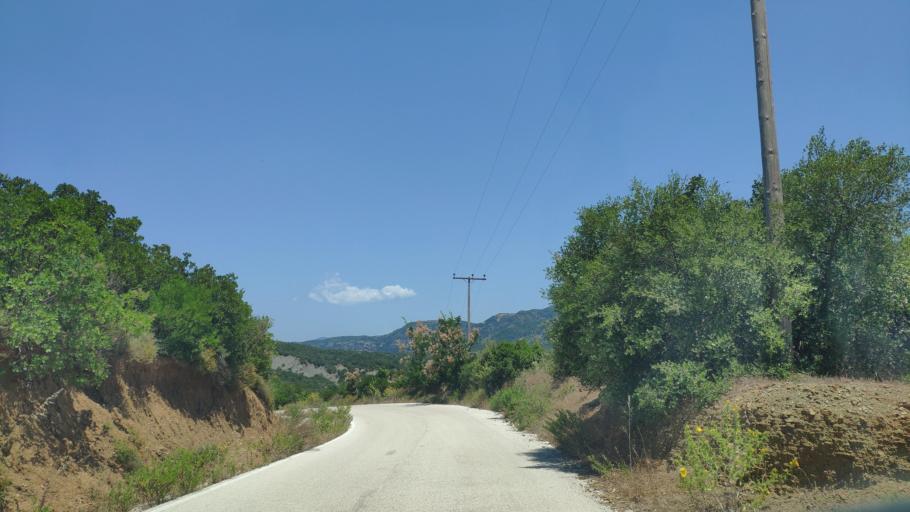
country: GR
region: West Greece
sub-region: Nomos Aitolias kai Akarnanias
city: Sardinia
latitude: 38.8826
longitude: 21.2804
